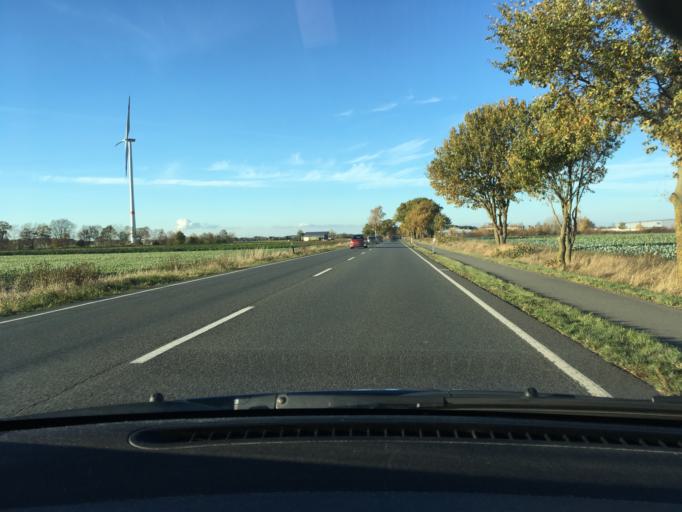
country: DE
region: Lower Saxony
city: Bardowick
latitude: 53.3071
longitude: 10.3731
